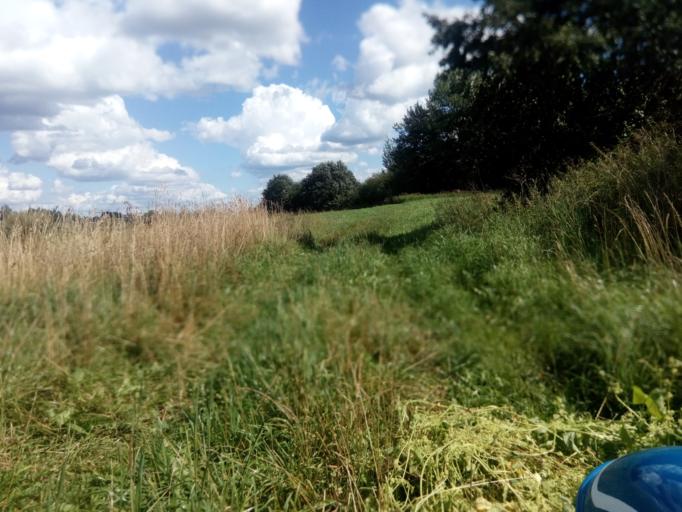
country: BY
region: Vitebsk
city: Dzisna
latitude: 55.6773
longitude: 28.3243
